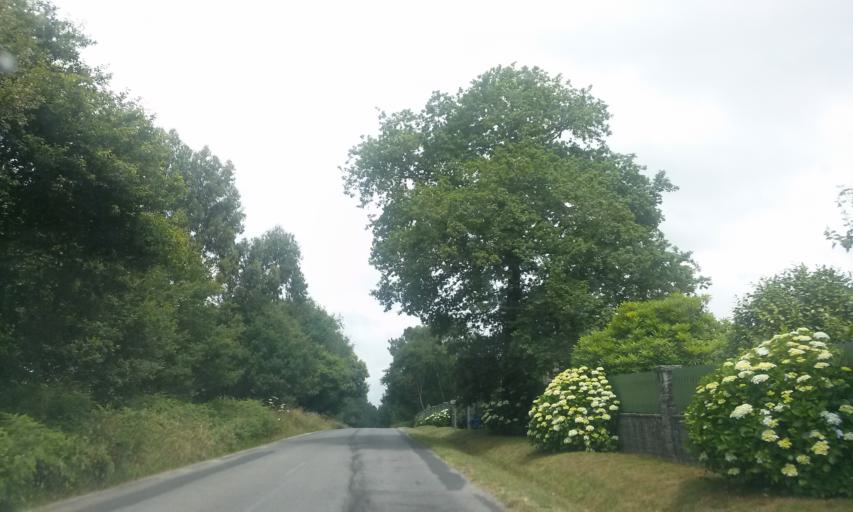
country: ES
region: Galicia
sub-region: Provincia de Lugo
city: Friol
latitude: 43.0931
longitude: -7.8088
